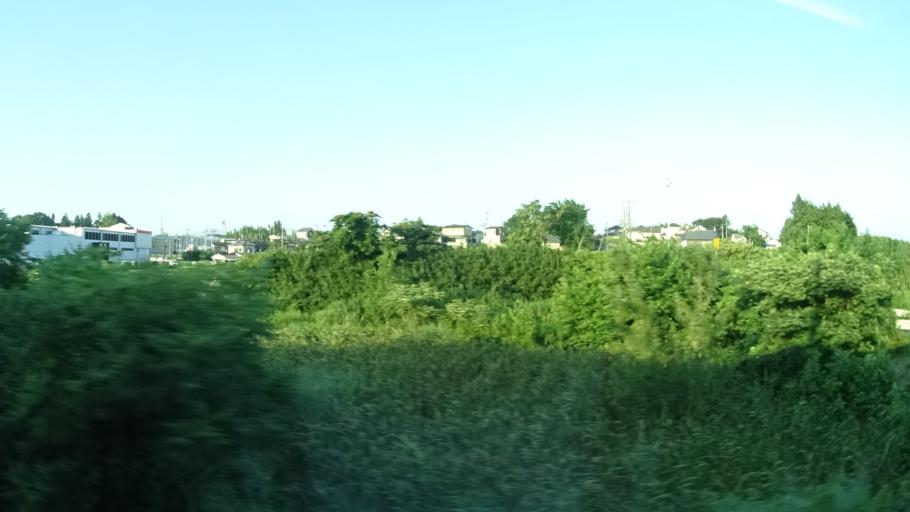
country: JP
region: Ibaraki
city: Ishioka
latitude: 36.1864
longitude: 140.2830
